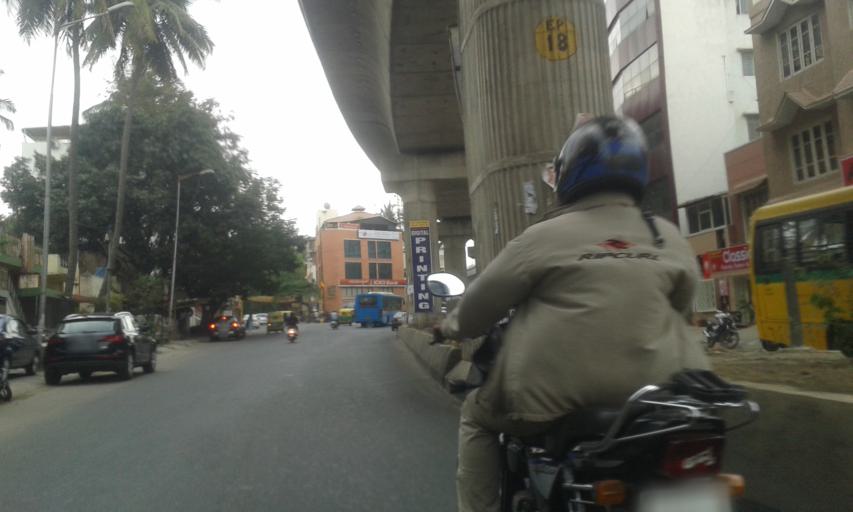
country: IN
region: Karnataka
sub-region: Bangalore Urban
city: Bangalore
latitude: 12.9177
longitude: 77.5768
